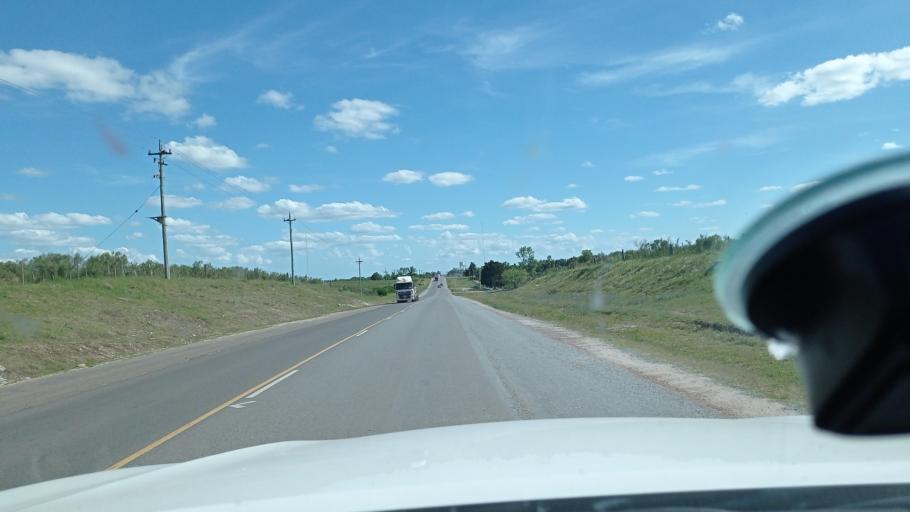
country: UY
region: Florida
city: Florida
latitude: -34.0789
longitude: -56.2350
